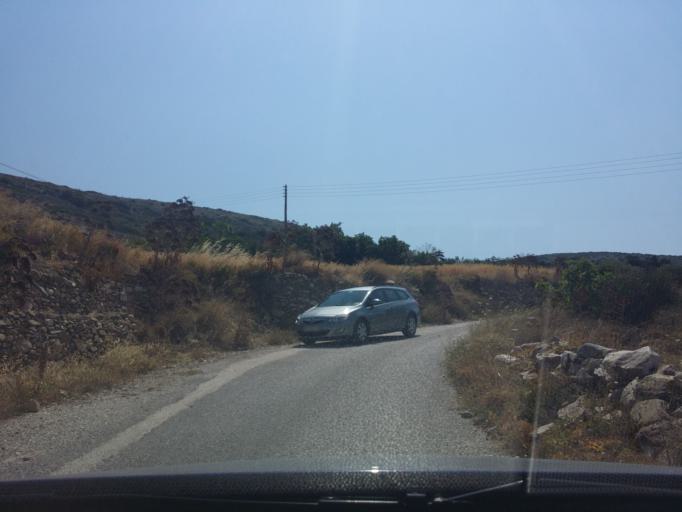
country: GR
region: South Aegean
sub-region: Nomos Kykladon
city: Paros
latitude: 37.0459
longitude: 25.1260
